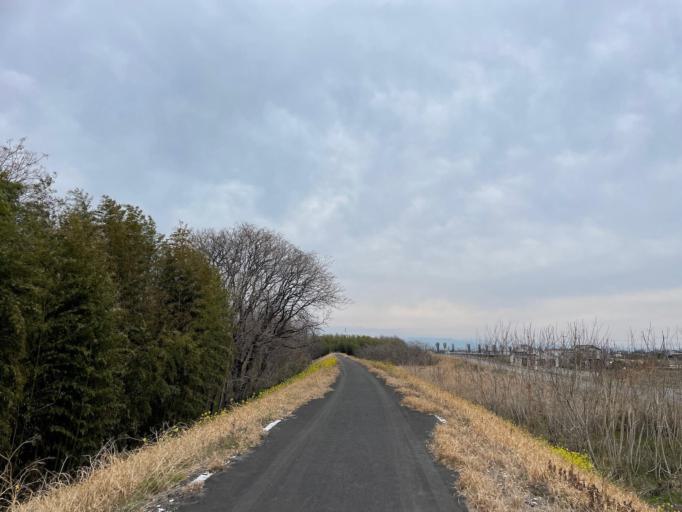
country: JP
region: Gunma
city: Fujioka
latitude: 36.2314
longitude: 139.0963
